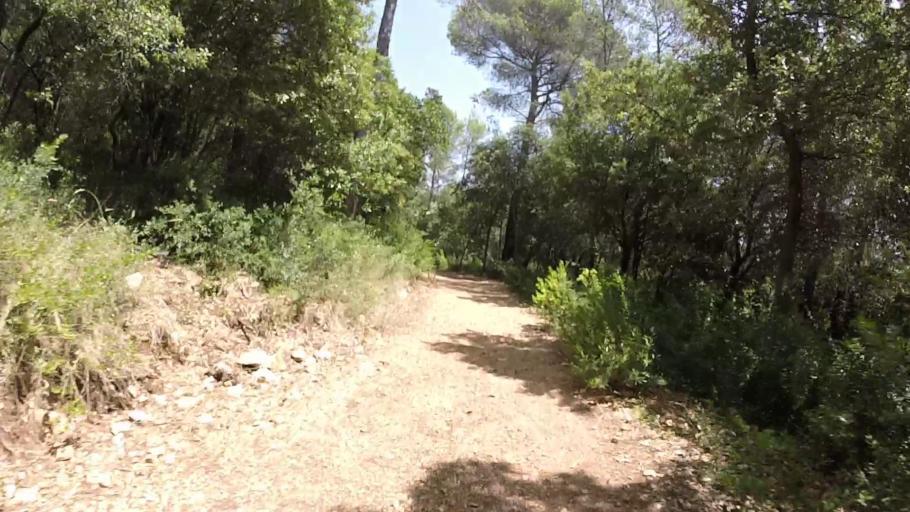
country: FR
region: Provence-Alpes-Cote d'Azur
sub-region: Departement des Alpes-Maritimes
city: Valbonne
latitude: 43.6211
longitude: 7.0117
